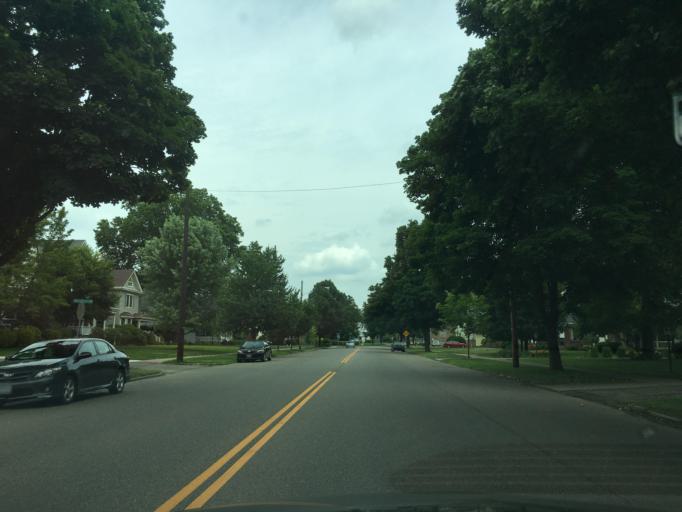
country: US
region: Ohio
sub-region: Tuscarawas County
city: New Philadelphia
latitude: 40.4957
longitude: -81.4439
